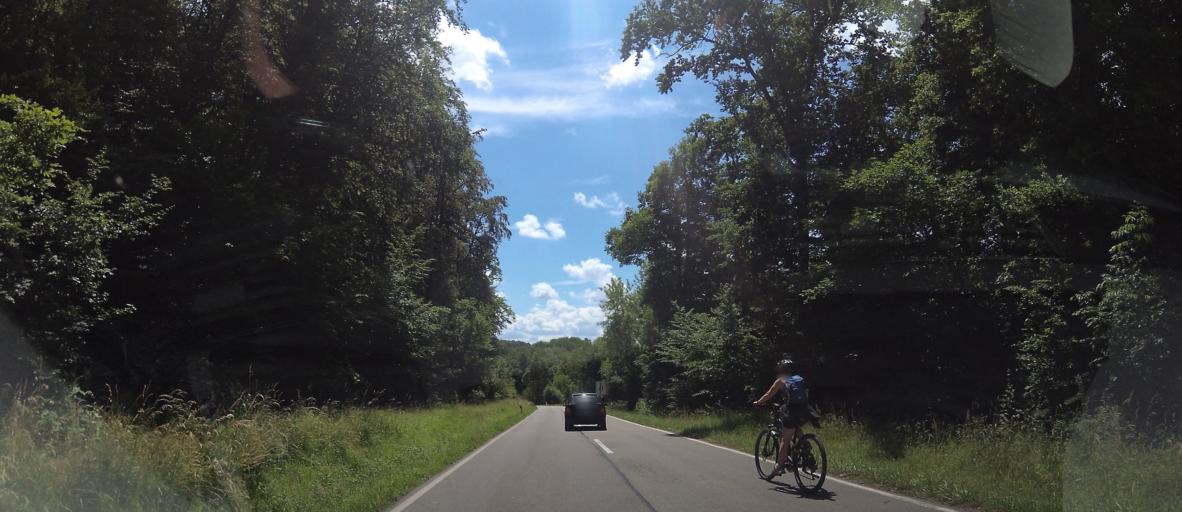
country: DE
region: Rheinland-Pfalz
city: Walshausen
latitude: 49.2155
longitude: 7.4754
